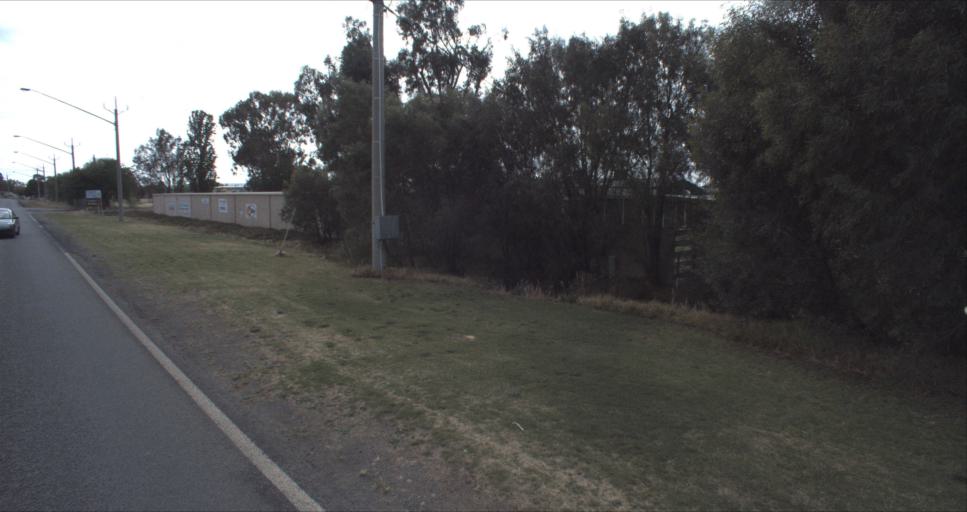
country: AU
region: New South Wales
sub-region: Leeton
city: Leeton
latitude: -34.5619
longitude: 146.4007
